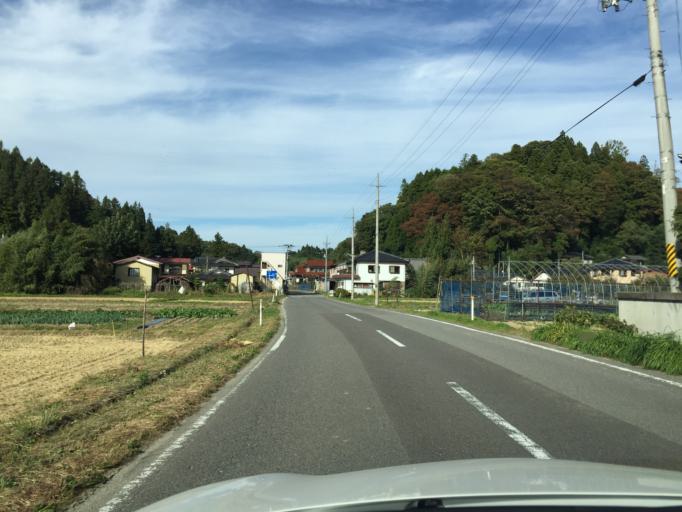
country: JP
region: Fukushima
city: Miharu
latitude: 37.3497
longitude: 140.5107
